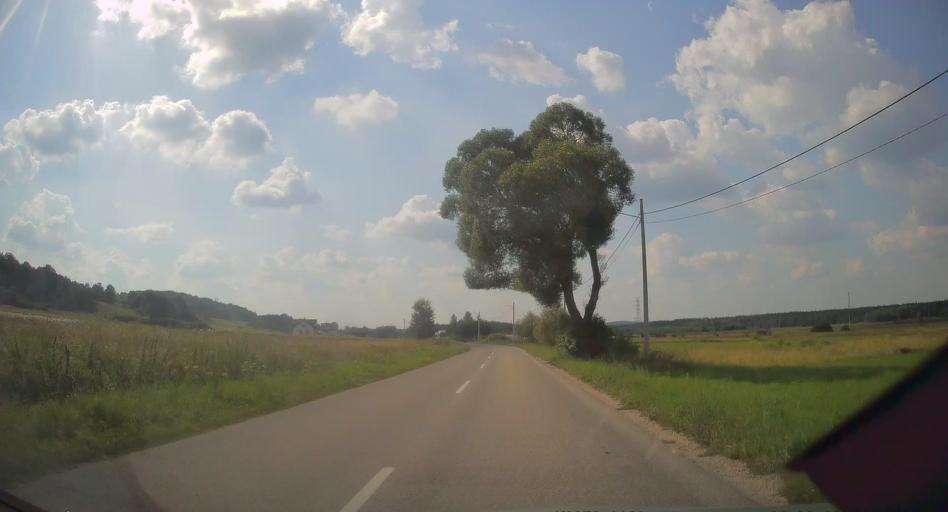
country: PL
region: Swietokrzyskie
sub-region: Powiat jedrzejowski
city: Malogoszcz
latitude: 50.8613
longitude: 20.3427
